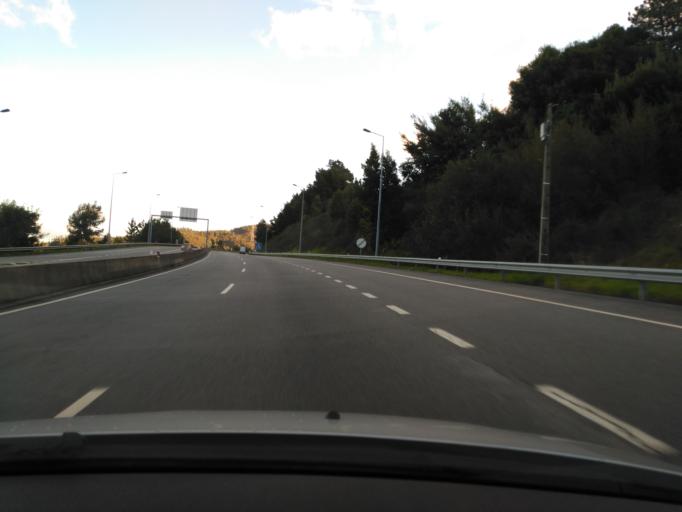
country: PT
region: Braga
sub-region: Fafe
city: Aroes
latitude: 41.4457
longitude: -8.2463
